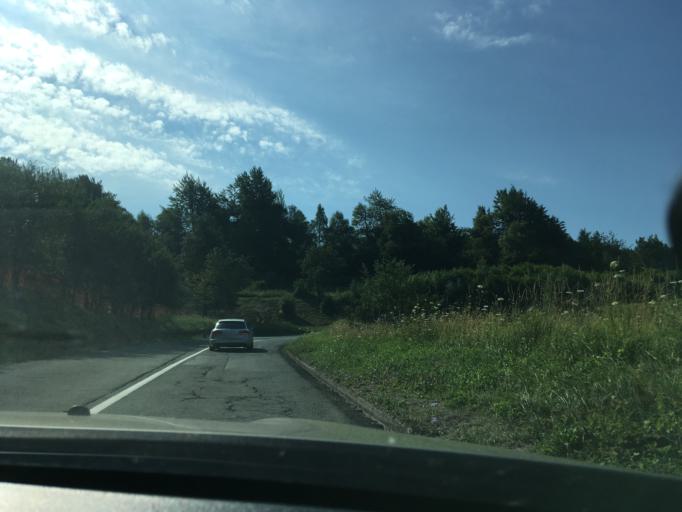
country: HR
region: Primorsko-Goranska
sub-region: Grad Delnice
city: Delnice
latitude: 45.4155
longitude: 14.8209
